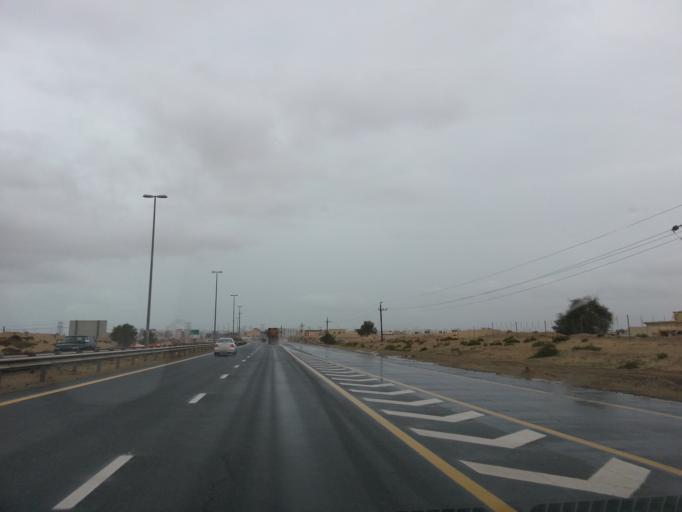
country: AE
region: Dubai
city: Dubai
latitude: 25.0632
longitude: 55.2207
